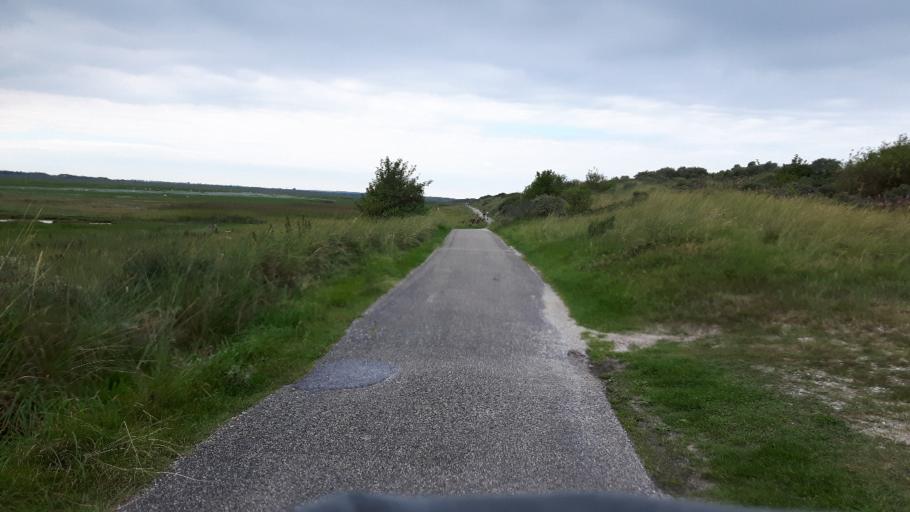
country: NL
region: Friesland
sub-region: Gemeente Dongeradeel
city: Holwerd
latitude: 53.4605
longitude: 5.8737
